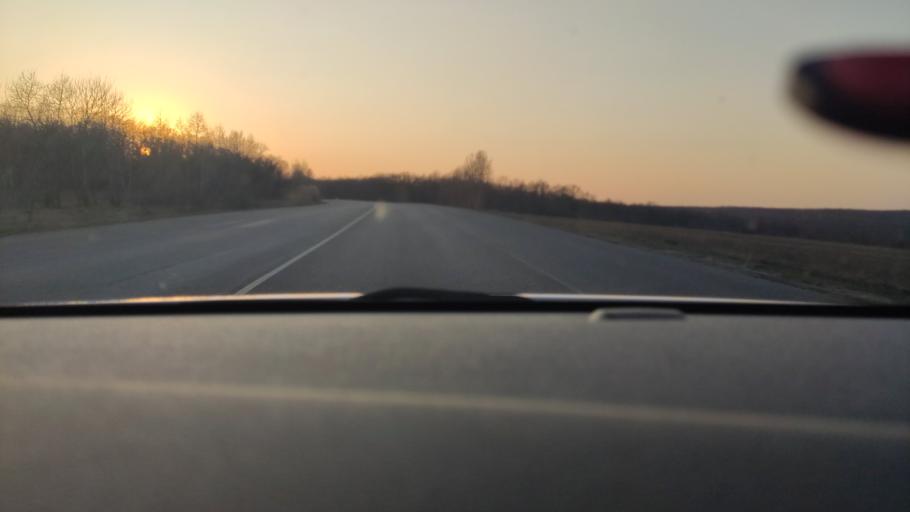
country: RU
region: Voronezj
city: Kolodeznyy
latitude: 51.3395
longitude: 39.0725
